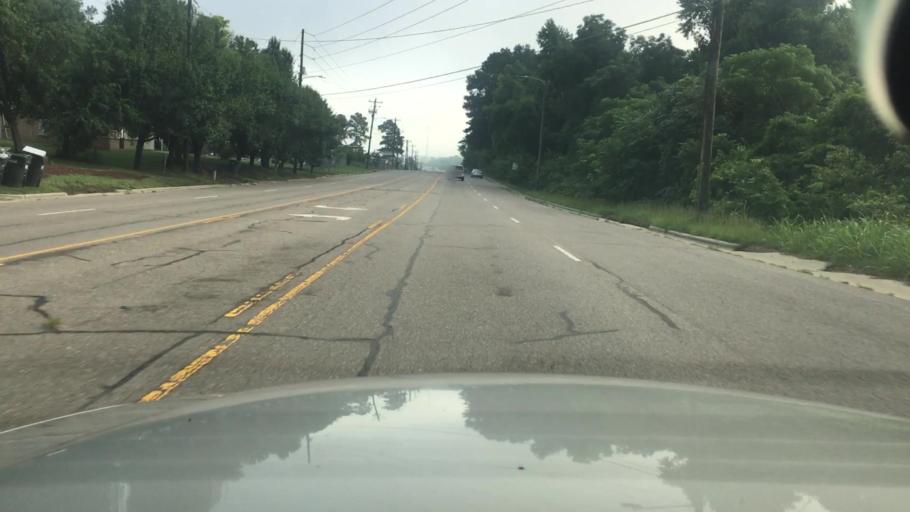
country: US
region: North Carolina
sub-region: Cumberland County
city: Fayetteville
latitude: 35.0291
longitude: -78.8881
